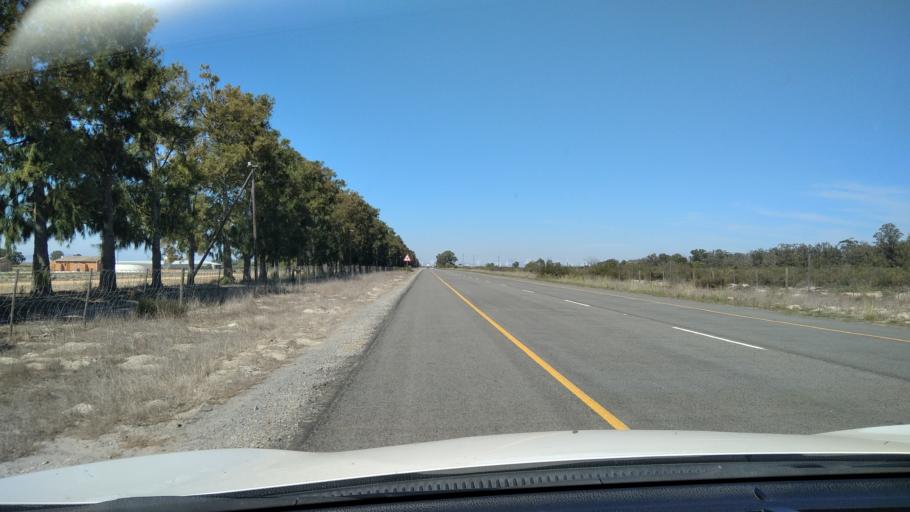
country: ZA
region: Western Cape
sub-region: West Coast District Municipality
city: Vredenburg
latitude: -33.0369
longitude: 18.3017
